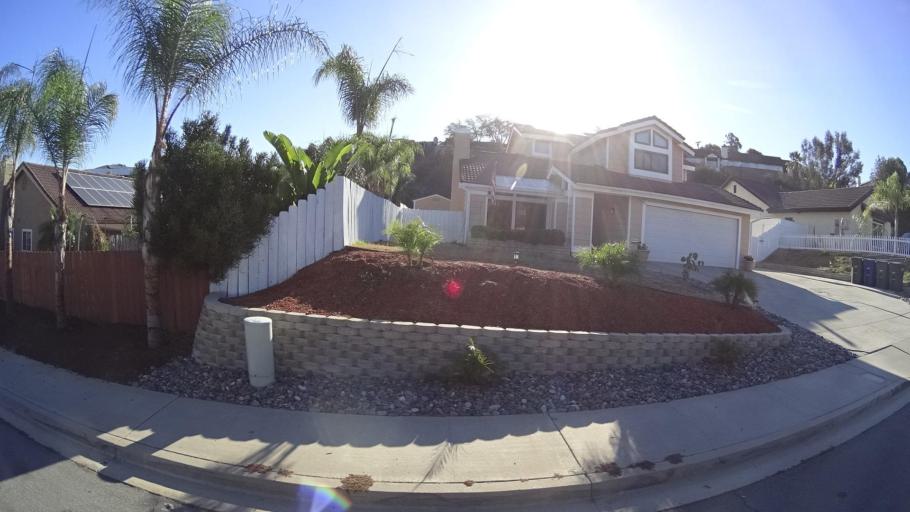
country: US
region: California
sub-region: San Diego County
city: Winter Gardens
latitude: 32.8345
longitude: -116.9119
